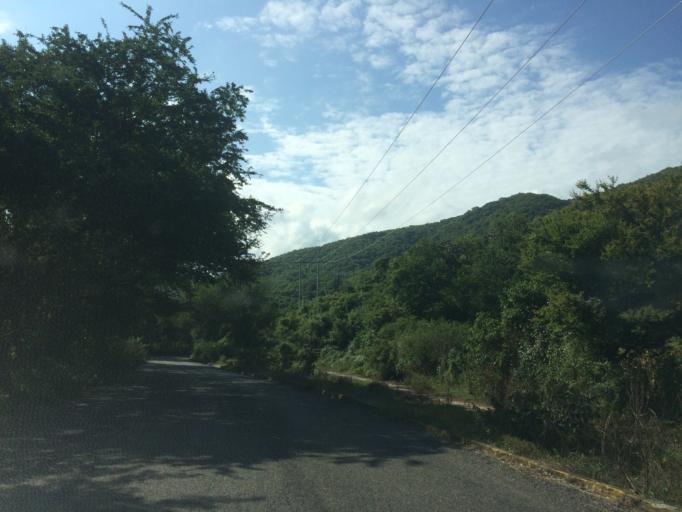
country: MX
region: Nayarit
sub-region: Ahuacatlan
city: Ahuacatlan
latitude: 21.0327
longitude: -104.4752
